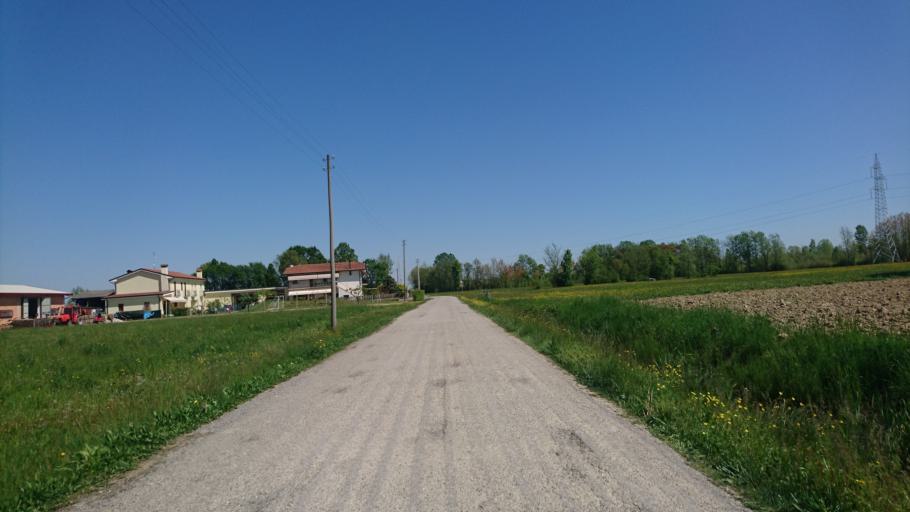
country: IT
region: Veneto
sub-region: Provincia di Treviso
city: Conscio
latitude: 45.6094
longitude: 12.2748
